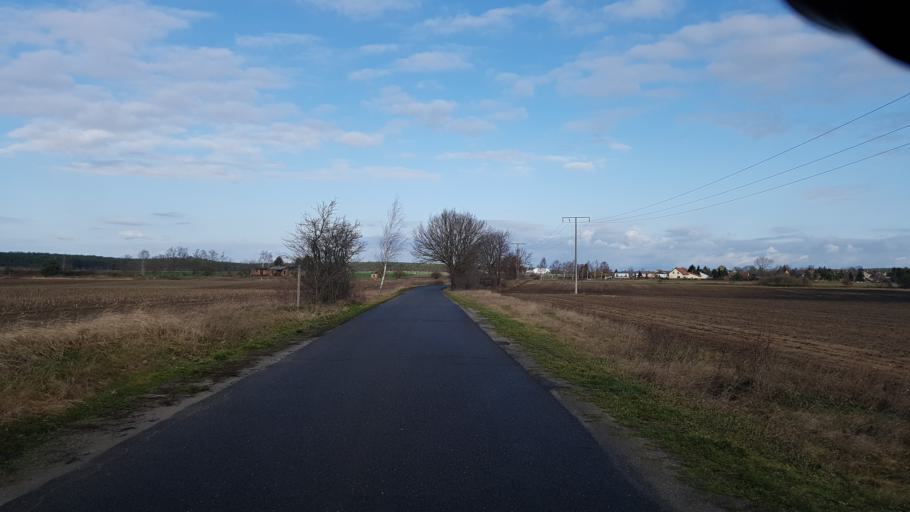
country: DE
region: Brandenburg
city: Schlieben
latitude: 51.7166
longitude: 13.3119
